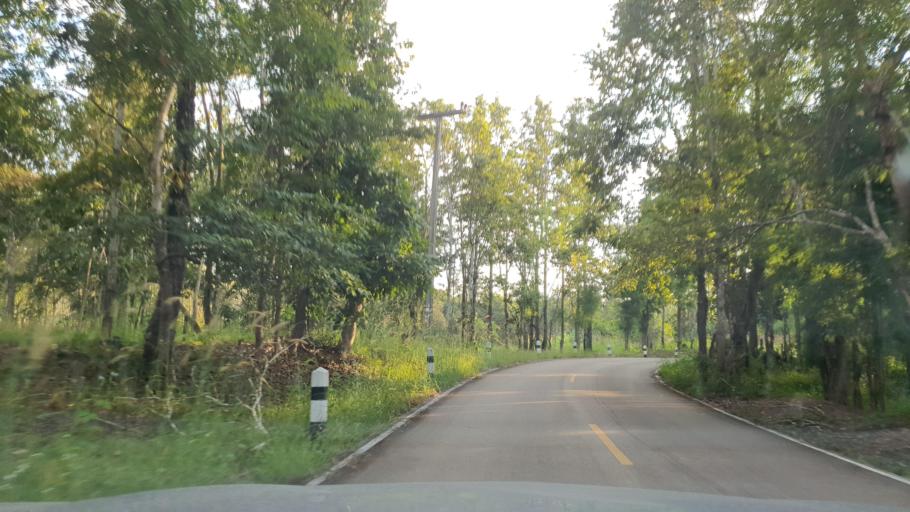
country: TH
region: Chiang Mai
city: Mae On
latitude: 18.8699
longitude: 99.2452
